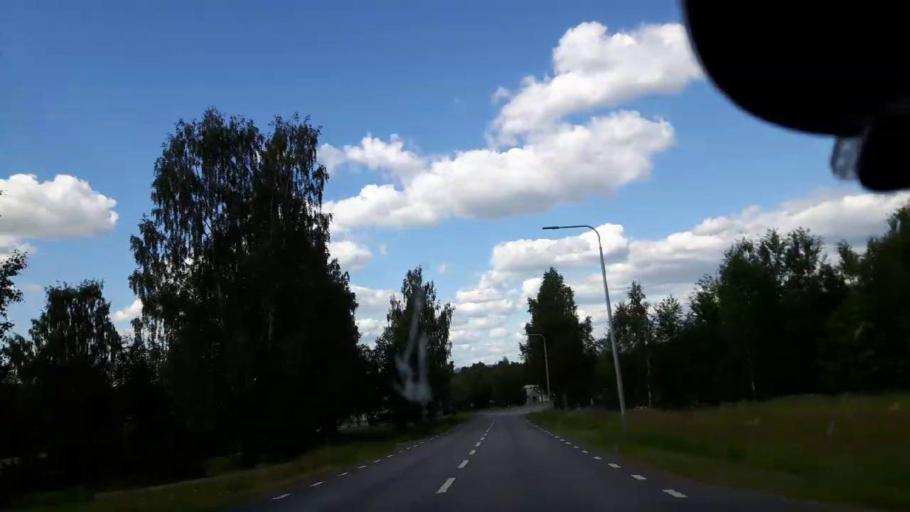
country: SE
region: Jaemtland
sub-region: Ragunda Kommun
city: Hammarstrand
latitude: 63.0047
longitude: 16.6710
